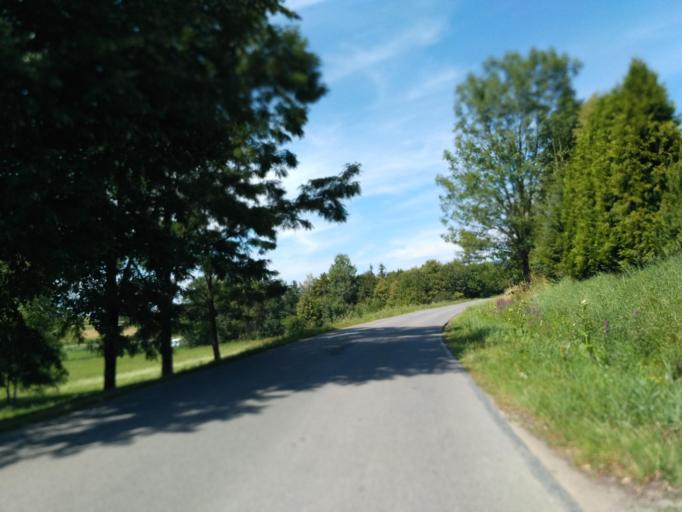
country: PL
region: Subcarpathian Voivodeship
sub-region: Powiat sanocki
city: Nowosielce-Gniewosz
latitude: 49.5459
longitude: 22.1085
